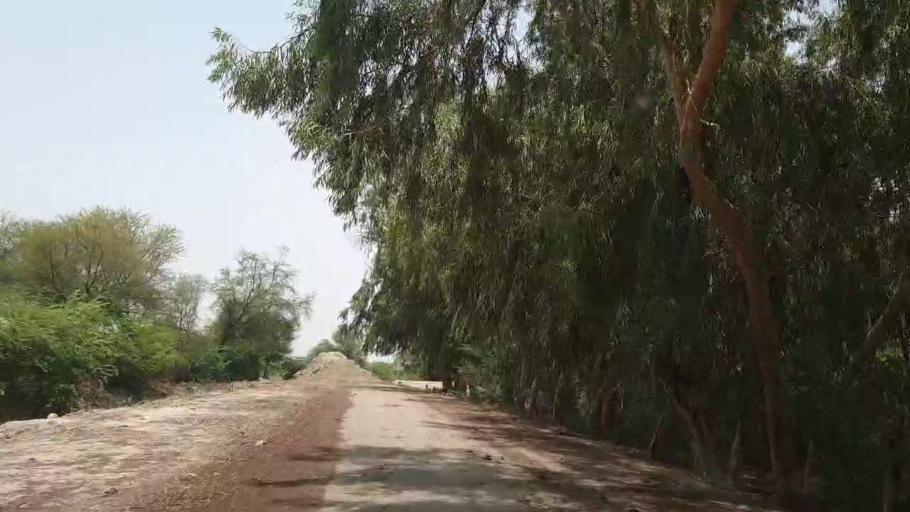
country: PK
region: Sindh
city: Sakrand
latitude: 26.0867
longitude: 68.2149
